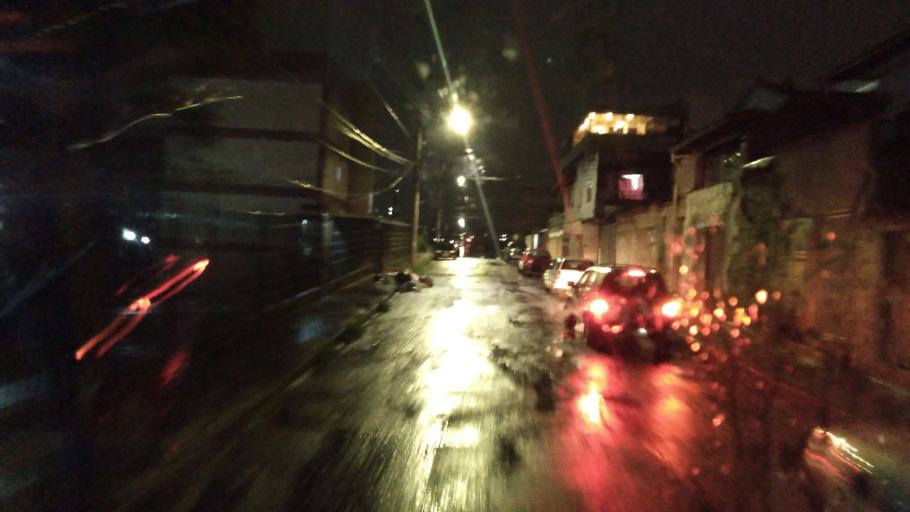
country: BR
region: Minas Gerais
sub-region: Belo Horizonte
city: Belo Horizonte
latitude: -19.9098
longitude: -43.9753
